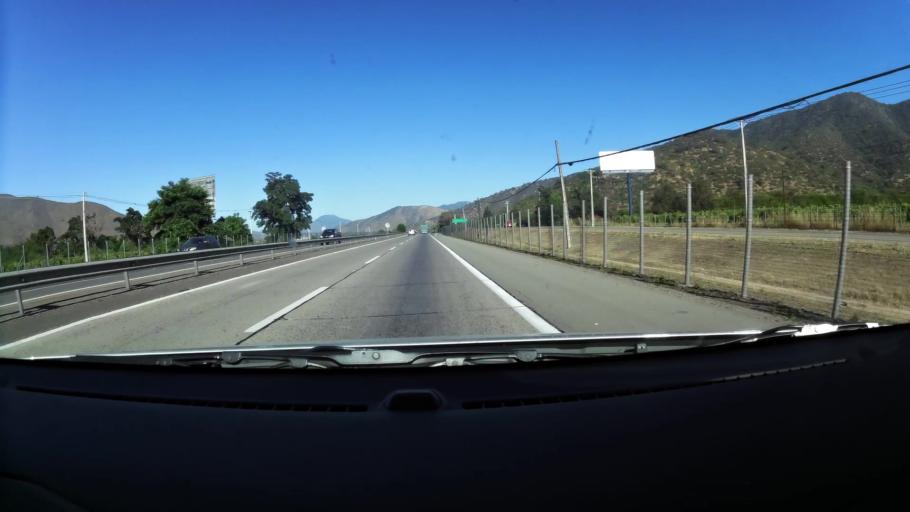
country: CL
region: Santiago Metropolitan
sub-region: Provincia de Chacabuco
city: Lampa
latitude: -33.4057
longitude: -71.0813
